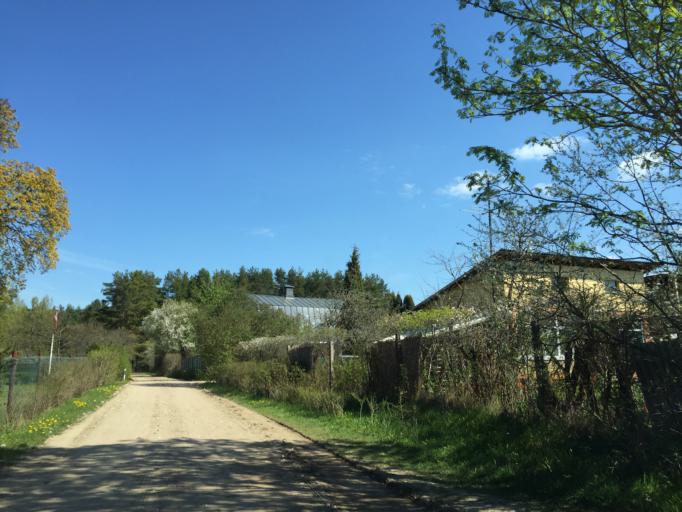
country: LV
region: Saulkrastu
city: Saulkrasti
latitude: 57.3127
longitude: 24.4333
